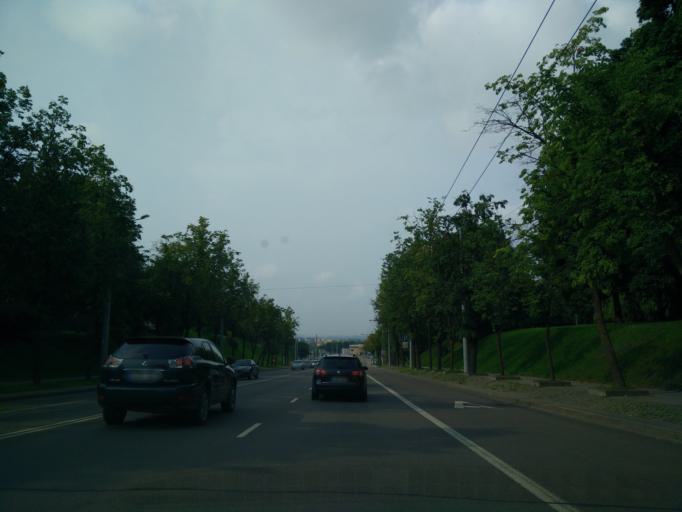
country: LT
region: Vilnius County
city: Naujamiestis
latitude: 54.6633
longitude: 25.2735
